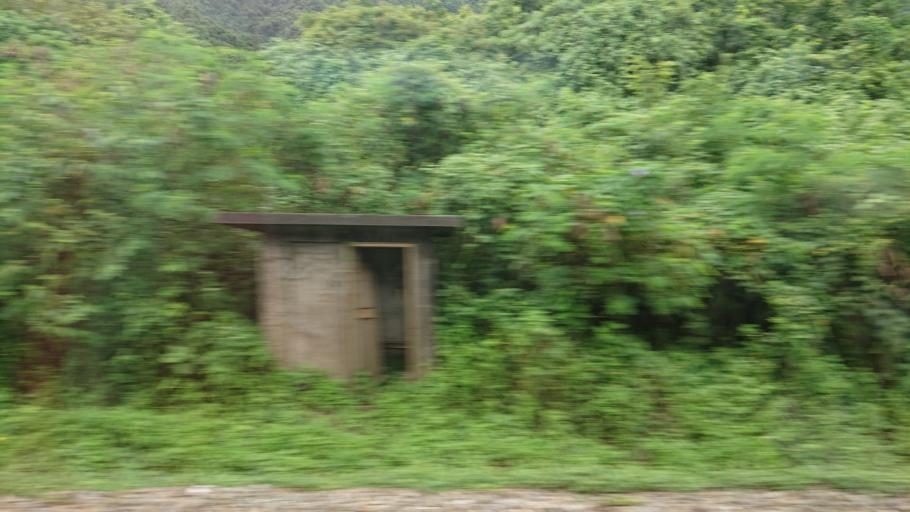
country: TW
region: Taiwan
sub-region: Keelung
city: Keelung
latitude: 24.9632
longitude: 121.9206
